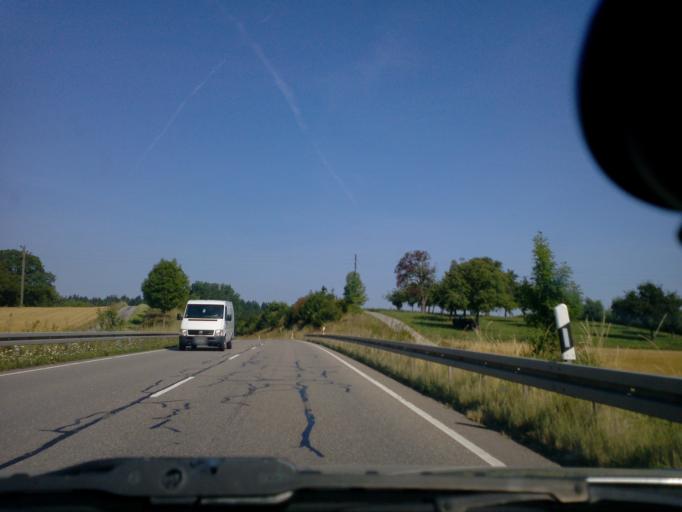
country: DE
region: Baden-Wuerttemberg
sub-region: Karlsruhe Region
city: Bretten
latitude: 49.0538
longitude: 8.7231
